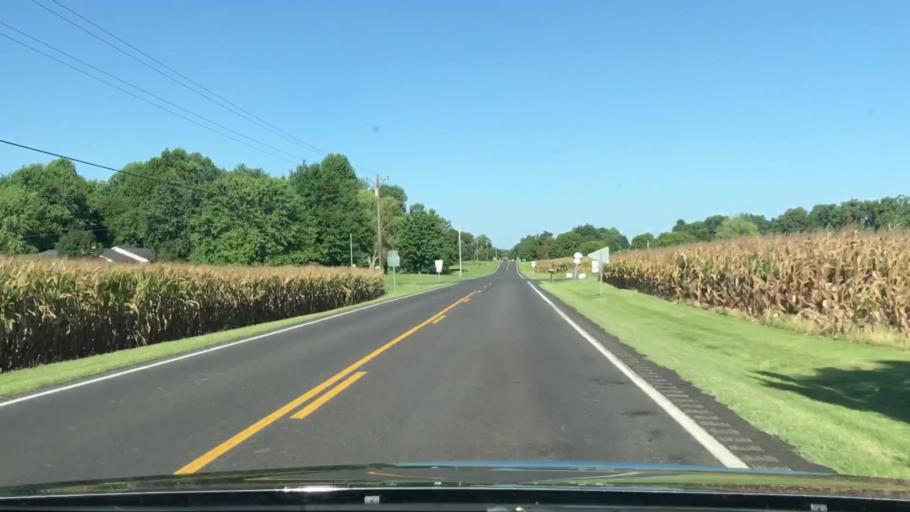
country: US
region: Kentucky
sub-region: Marshall County
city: Benton
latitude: 36.7668
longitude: -88.4296
